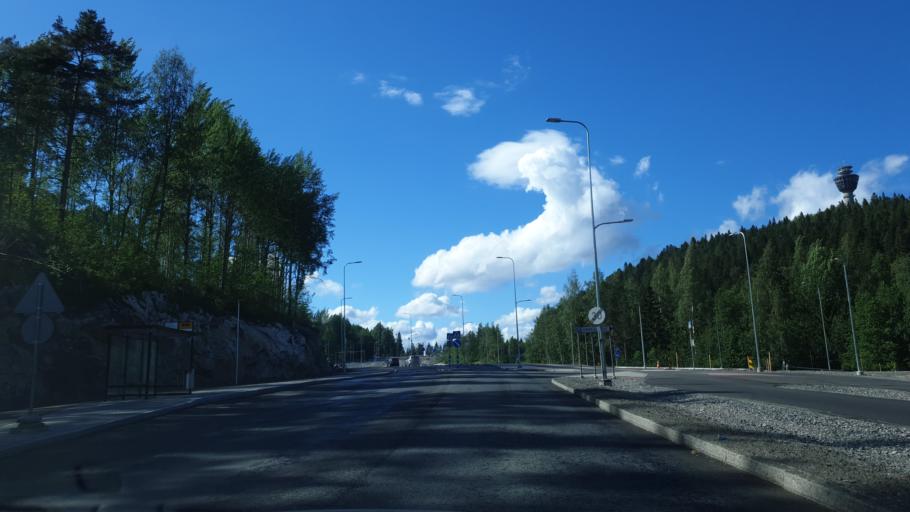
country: FI
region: Northern Savo
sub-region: Kuopio
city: Kuopio
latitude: 62.9032
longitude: 27.6596
